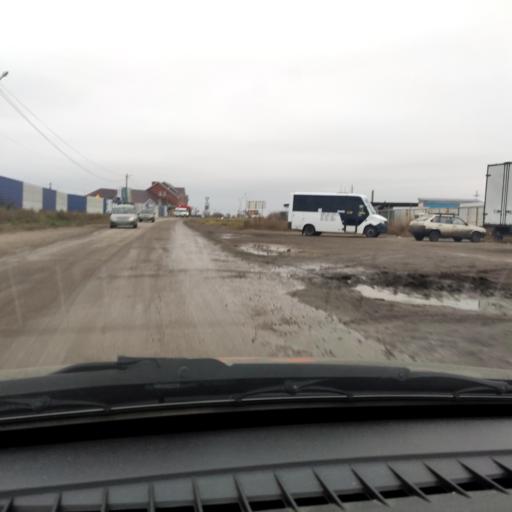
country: RU
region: Samara
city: Podstepki
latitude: 53.5153
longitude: 49.2185
